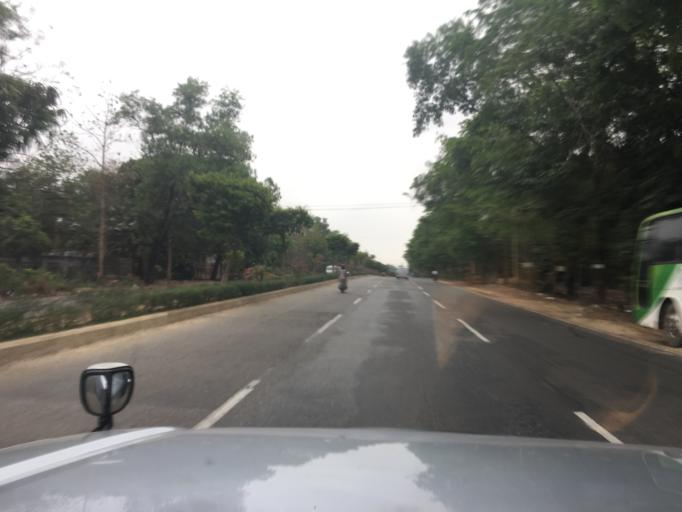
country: MM
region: Bago
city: Bago
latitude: 17.2411
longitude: 96.4639
